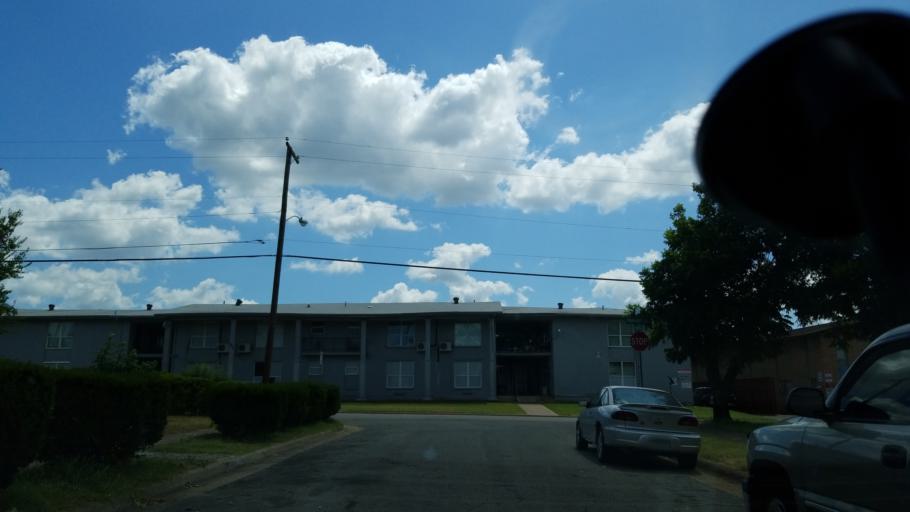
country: US
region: Texas
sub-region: Dallas County
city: Cockrell Hill
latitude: 32.7022
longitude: -96.8426
